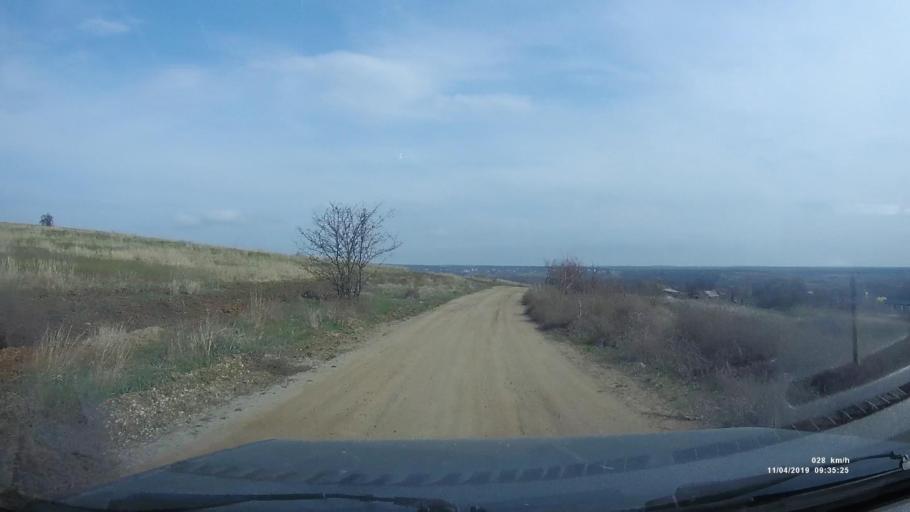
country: RU
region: Rostov
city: Staraya Stanitsa
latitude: 48.2723
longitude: 40.3717
